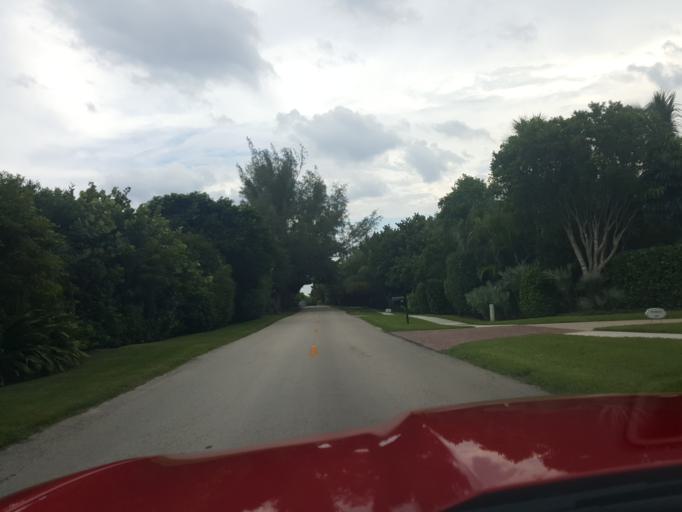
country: US
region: Florida
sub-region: Martin County
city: Hobe Sound
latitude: 27.0240
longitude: -80.0973
